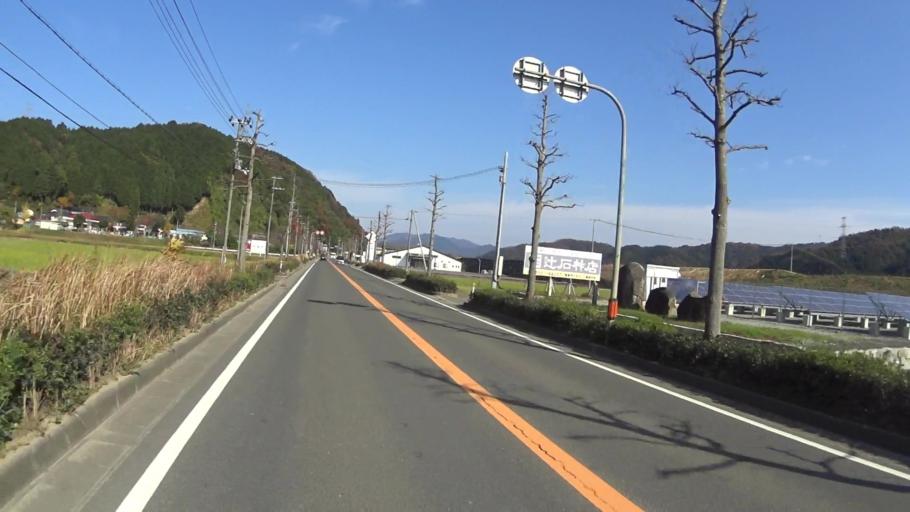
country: JP
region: Kyoto
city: Maizuru
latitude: 35.4361
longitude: 135.2542
